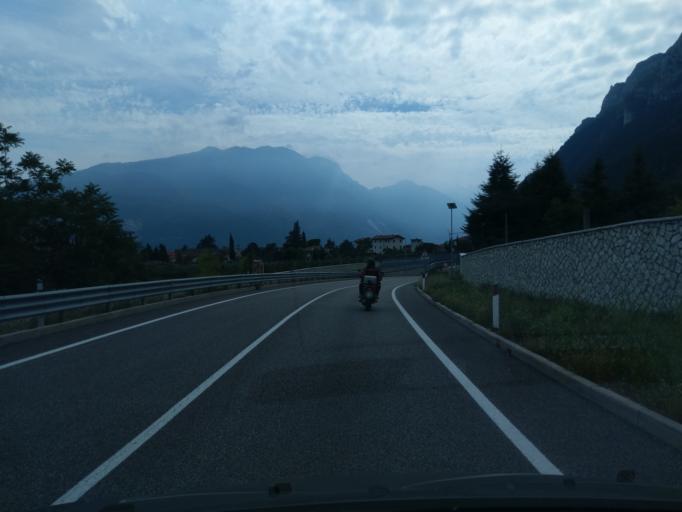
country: IT
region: Trentino-Alto Adige
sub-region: Provincia di Trento
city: Riva del Garda
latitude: 45.8957
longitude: 10.8383
